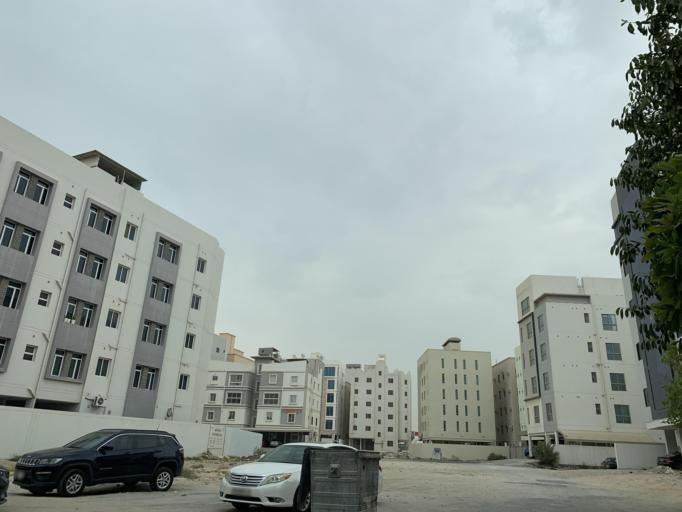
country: BH
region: Northern
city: Madinat `Isa
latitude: 26.1835
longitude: 50.4786
